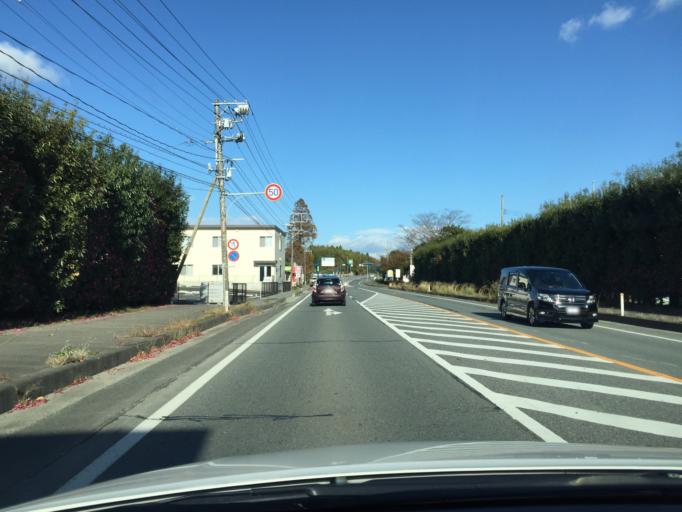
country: JP
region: Fukushima
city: Iwaki
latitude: 37.2309
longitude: 141.0000
